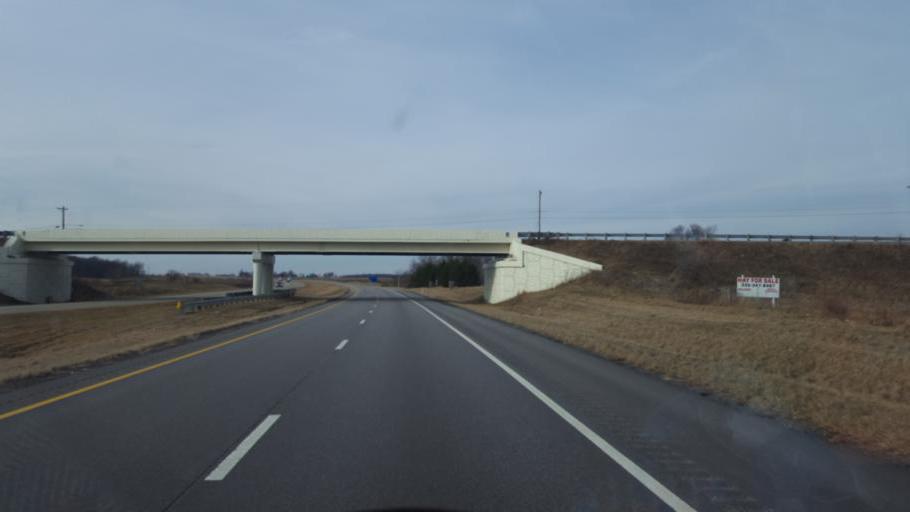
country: US
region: Ohio
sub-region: Wayne County
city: Apple Creek
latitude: 40.8049
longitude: -81.8232
